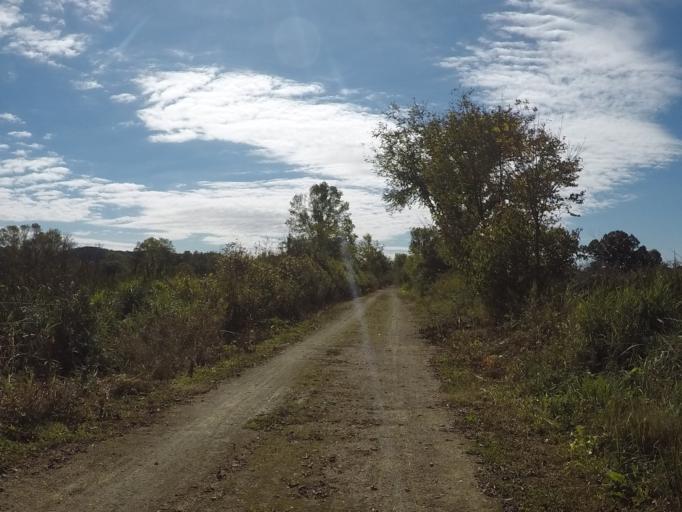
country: US
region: Wisconsin
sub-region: Richland County
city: Richland Center
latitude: 43.2716
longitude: -90.3096
